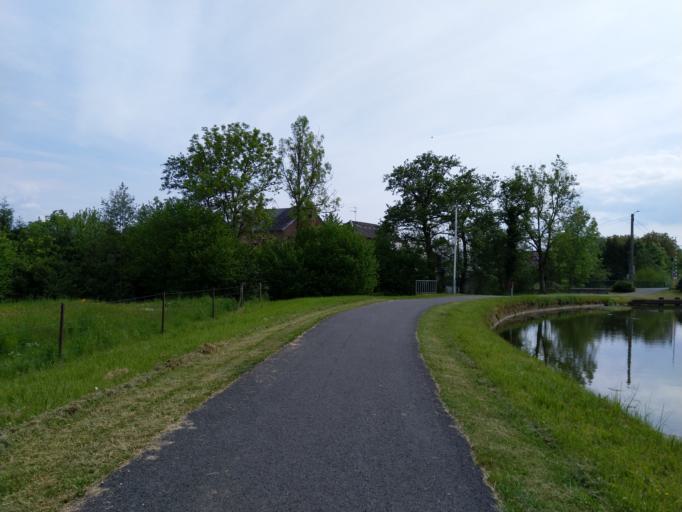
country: FR
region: Picardie
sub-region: Departement de l'Aisne
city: Etreux
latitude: 49.9717
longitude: 3.6287
